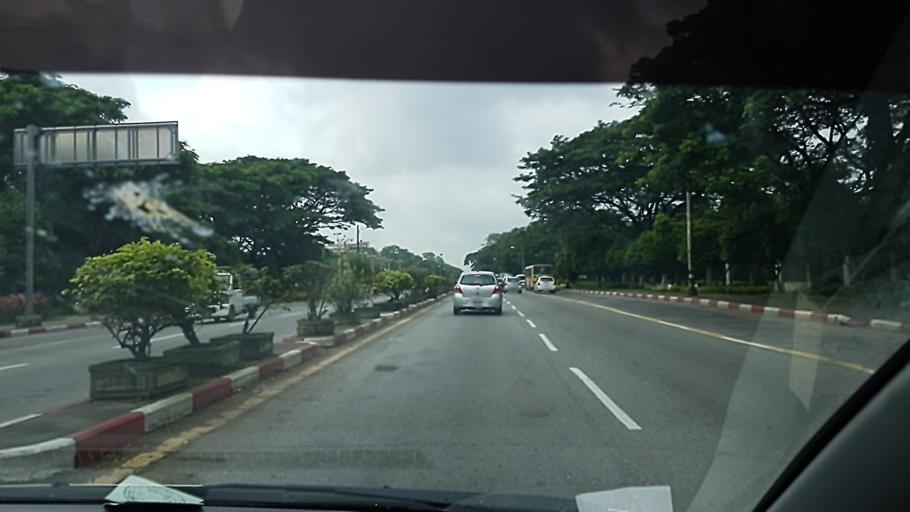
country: MM
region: Yangon
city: Yangon
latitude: 16.7975
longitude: 96.1390
